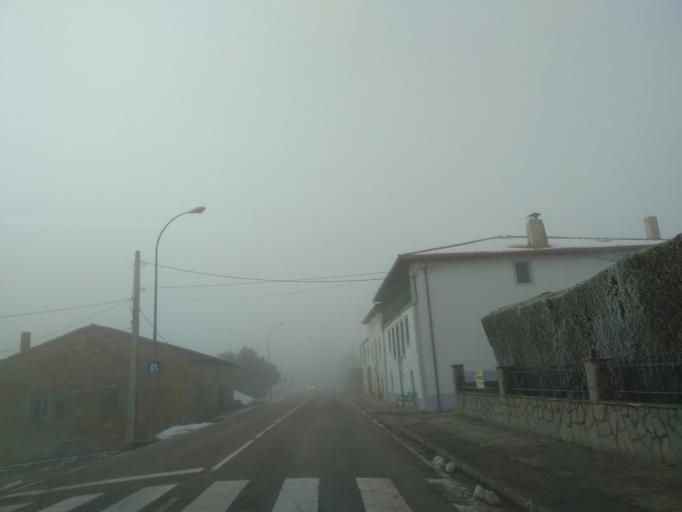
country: ES
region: Castille and Leon
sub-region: Provincia de Burgos
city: Espinosa de los Monteros
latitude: 43.0223
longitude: -3.5084
